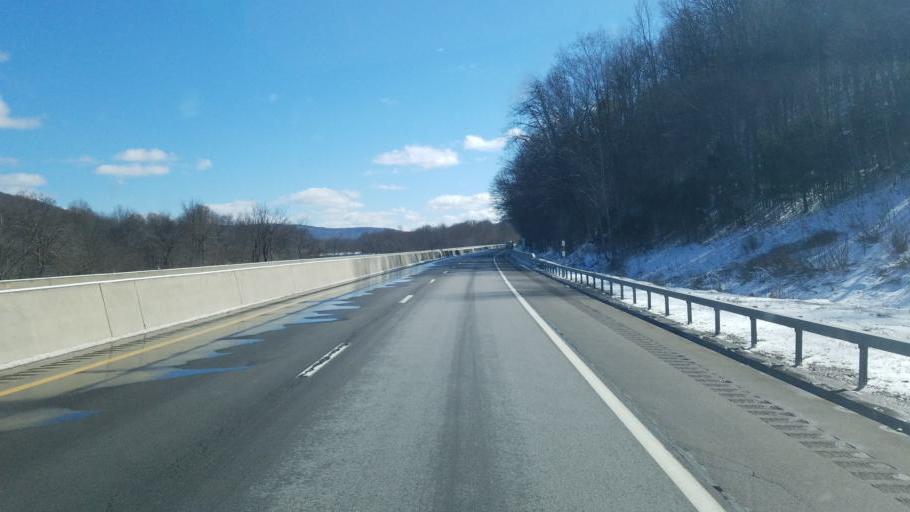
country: US
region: New York
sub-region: Cattaraugus County
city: Salamanca
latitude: 42.1209
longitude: -78.6646
